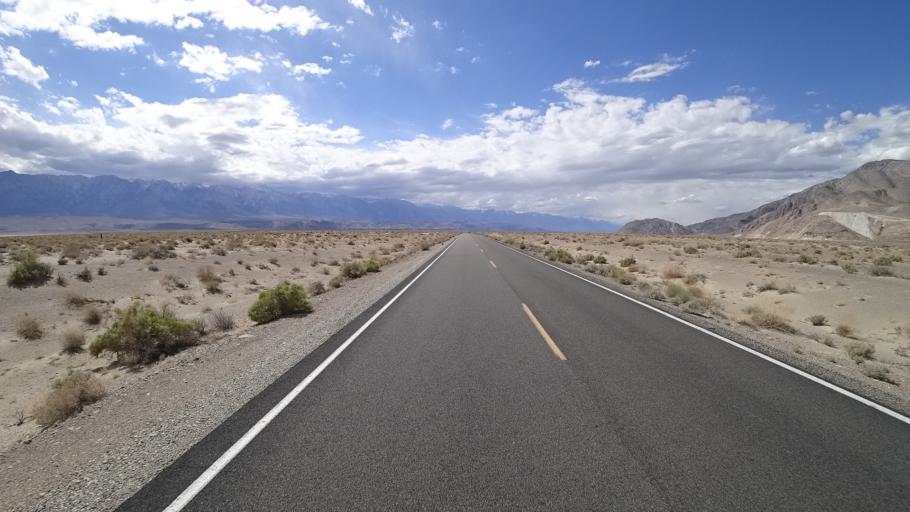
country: US
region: California
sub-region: Inyo County
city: Lone Pine
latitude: 36.5530
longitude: -117.9547
